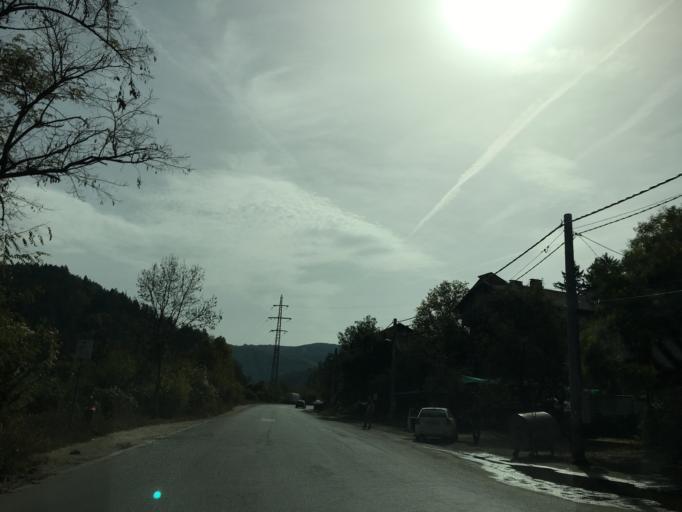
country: BG
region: Sofia-Capital
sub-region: Stolichna Obshtina
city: Sofia
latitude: 42.5823
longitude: 23.4244
